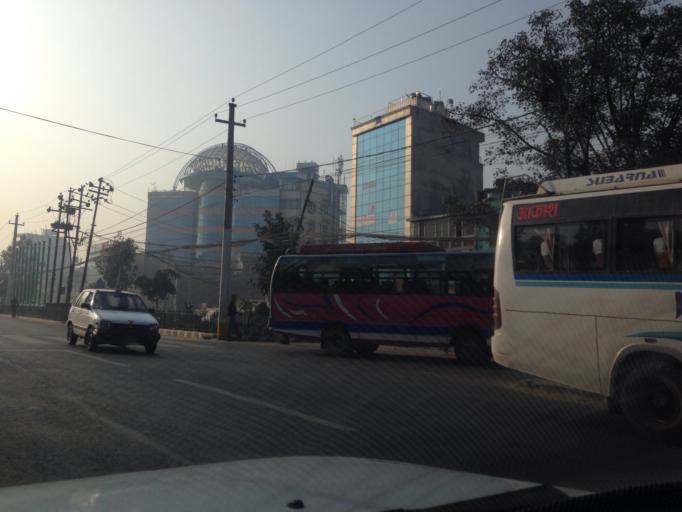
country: NP
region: Central Region
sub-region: Bagmati Zone
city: Kathmandu
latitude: 27.7015
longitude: 85.3531
